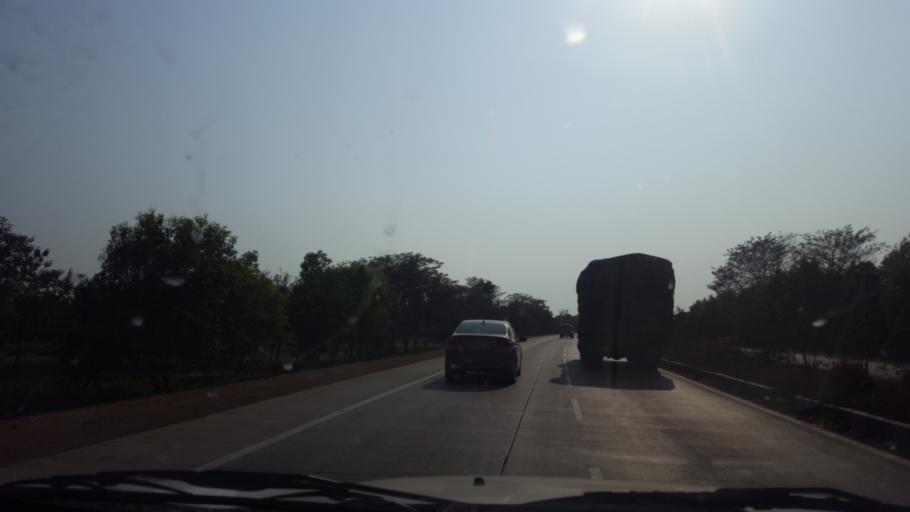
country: IN
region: Andhra Pradesh
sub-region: Vishakhapatnam
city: Elamanchili
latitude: 17.5328
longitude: 82.8262
